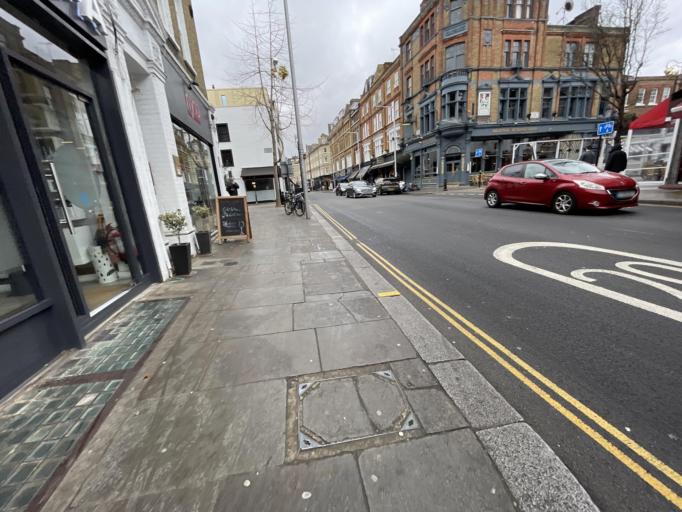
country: GB
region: England
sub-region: Greater London
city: Chelsea
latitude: 51.4860
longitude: -0.1809
